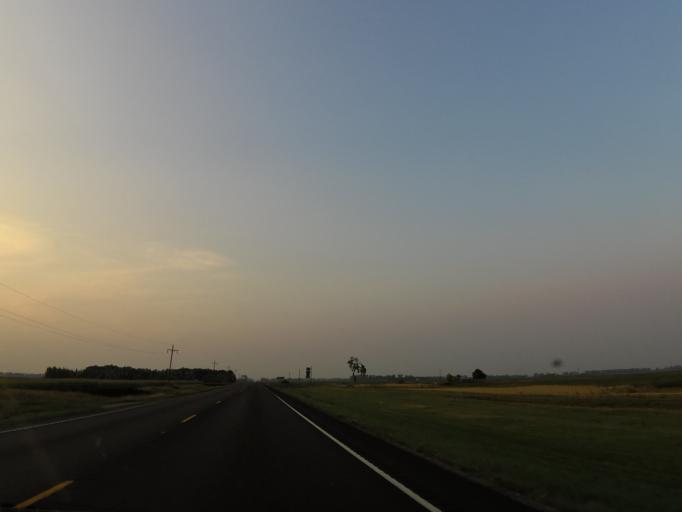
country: US
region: North Dakota
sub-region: Walsh County
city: Park River
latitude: 48.3079
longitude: -97.6224
